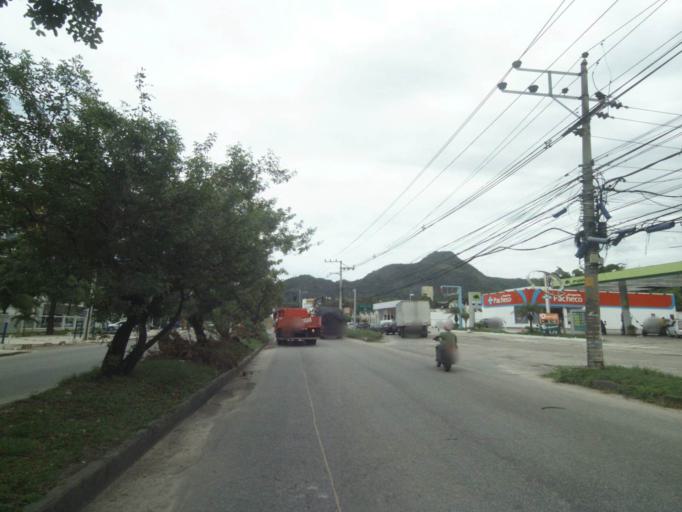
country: BR
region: Rio de Janeiro
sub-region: Nilopolis
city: Nilopolis
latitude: -22.9670
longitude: -43.4126
